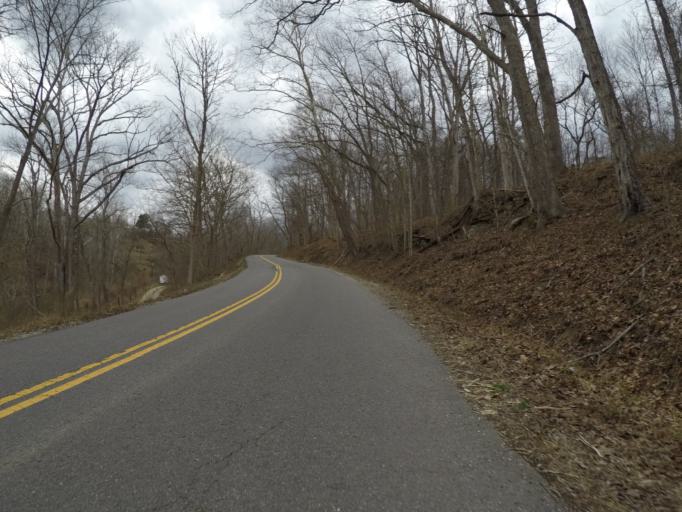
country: US
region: Ohio
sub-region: Lawrence County
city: Burlington
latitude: 38.4300
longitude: -82.5254
